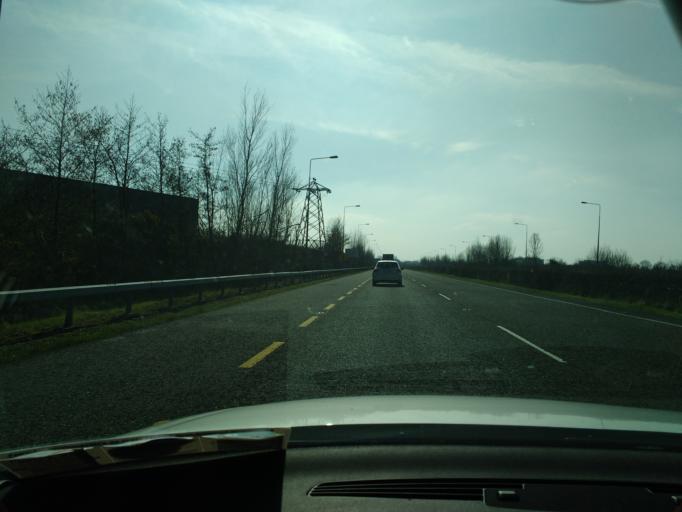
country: IE
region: Munster
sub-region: An Clar
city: Shannon
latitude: 52.7196
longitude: -8.8798
